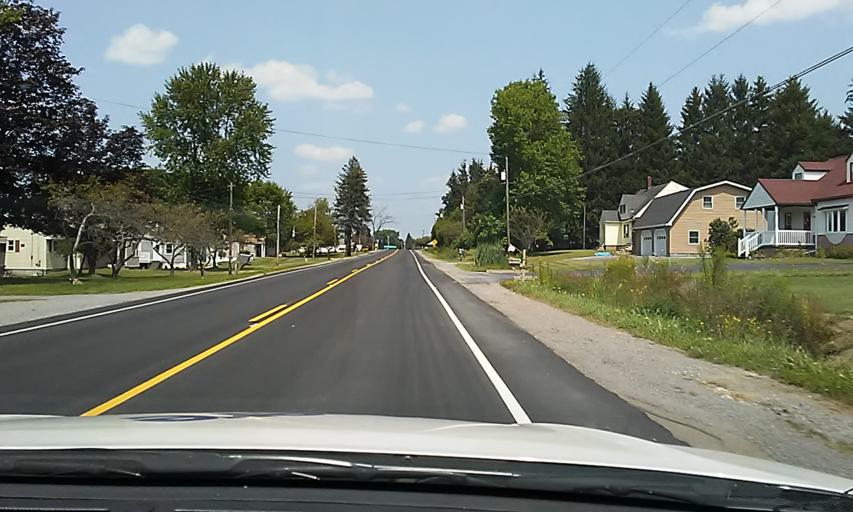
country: US
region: Pennsylvania
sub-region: Elk County
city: Saint Marys
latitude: 41.4402
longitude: -78.5055
